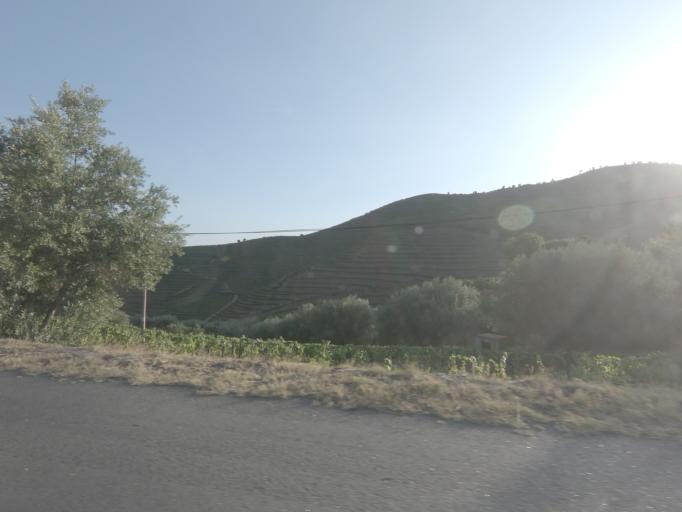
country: PT
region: Vila Real
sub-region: Sabrosa
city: Vilela
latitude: 41.1926
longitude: -7.6392
